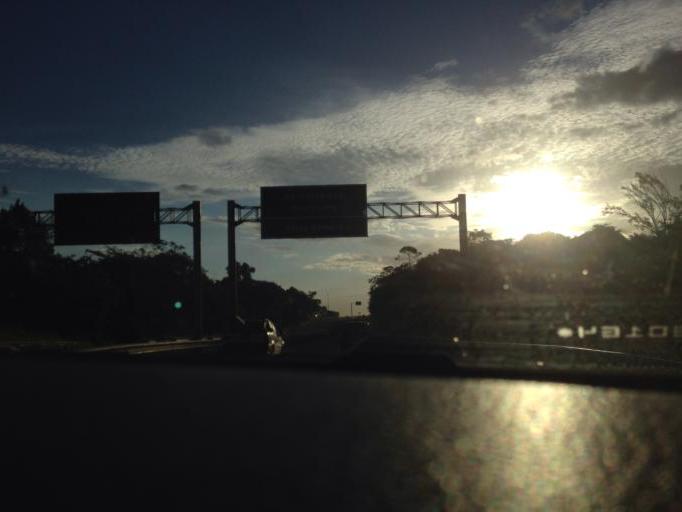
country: BR
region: Espirito Santo
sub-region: Viana
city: Viana
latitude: -20.5210
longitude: -40.3709
